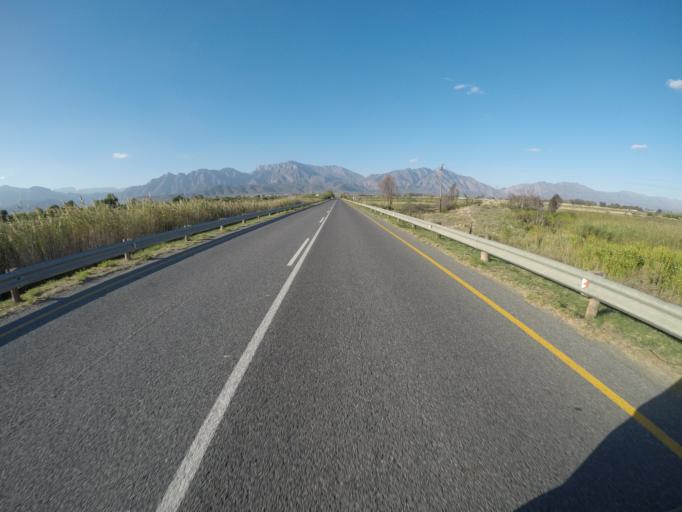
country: ZA
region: Western Cape
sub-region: Cape Winelands District Municipality
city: Worcester
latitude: -33.6794
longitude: 19.5275
